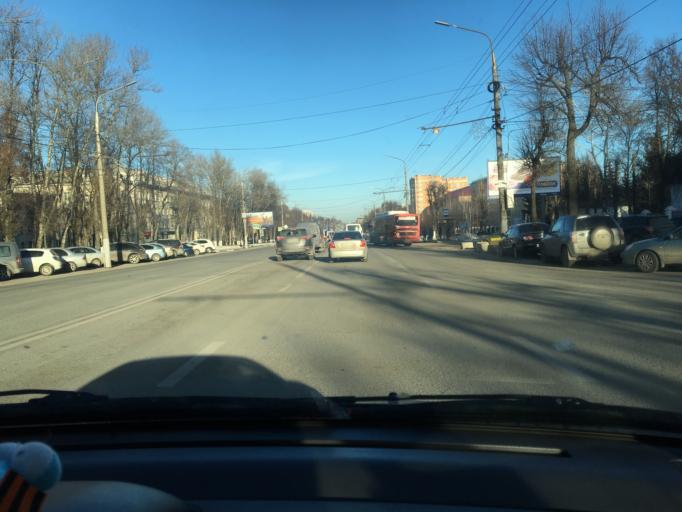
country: RU
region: Tula
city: Mendeleyevskiy
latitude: 54.1685
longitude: 37.5906
